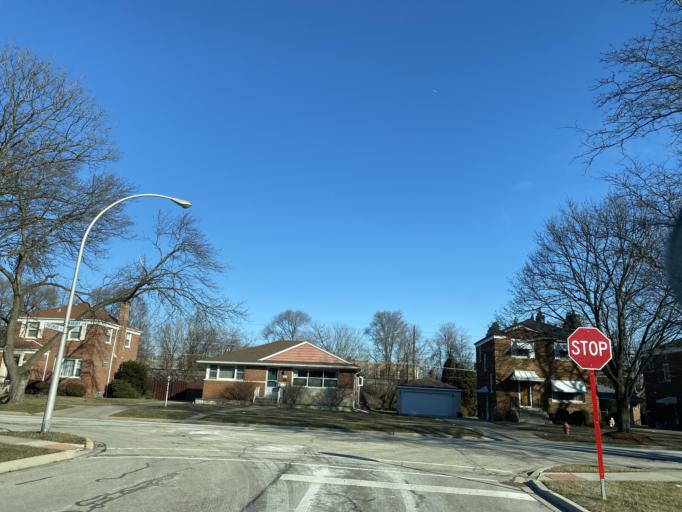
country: US
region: Illinois
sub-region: Cook County
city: Westchester
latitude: 41.8619
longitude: -87.8737
